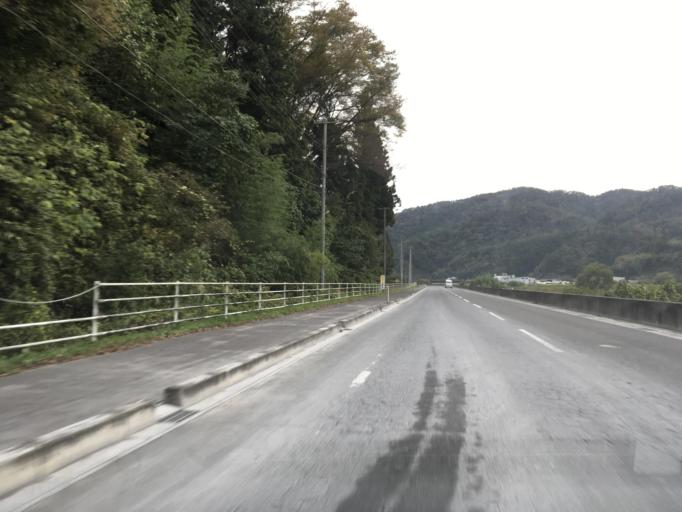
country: JP
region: Iwate
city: Ichinoseki
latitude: 38.9809
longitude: 141.2456
